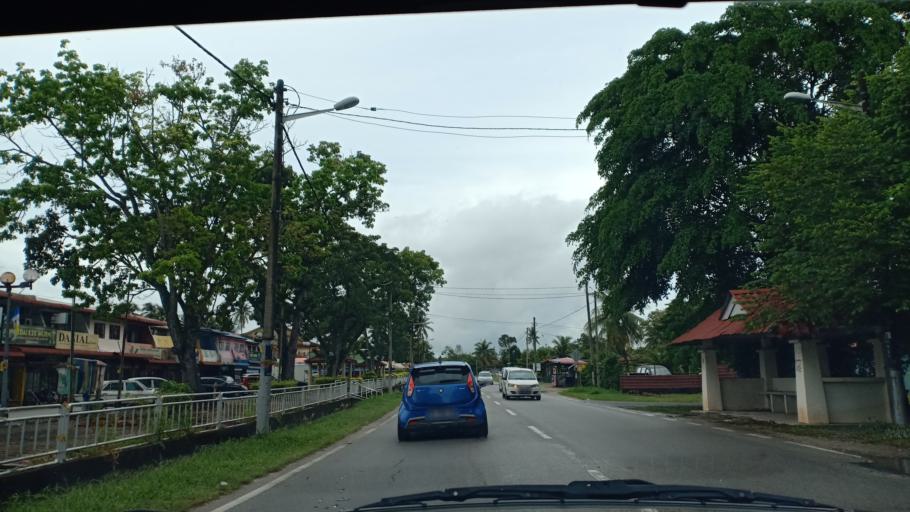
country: MY
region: Penang
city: Kepala Batas
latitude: 5.4937
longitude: 100.4511
